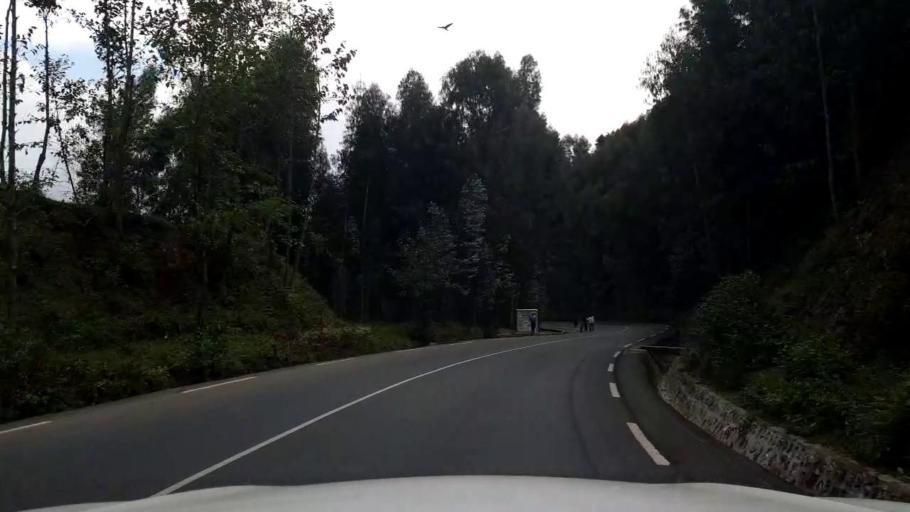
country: RW
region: Northern Province
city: Musanze
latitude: -1.6748
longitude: 29.5169
